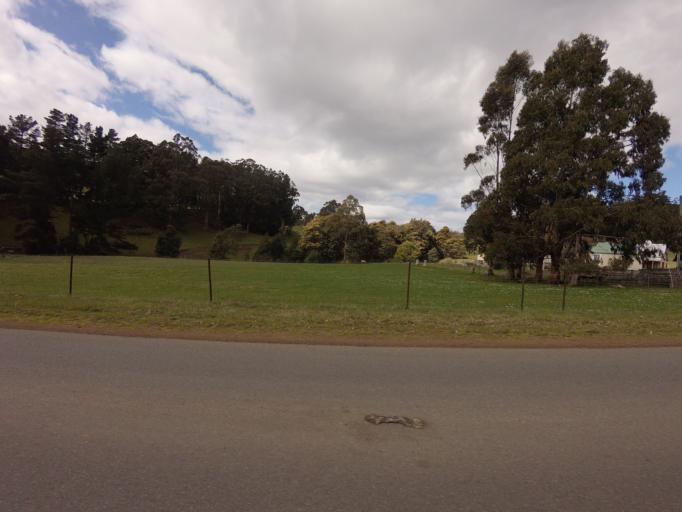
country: AU
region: Tasmania
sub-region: Huon Valley
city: Geeveston
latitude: -43.2410
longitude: 146.9919
